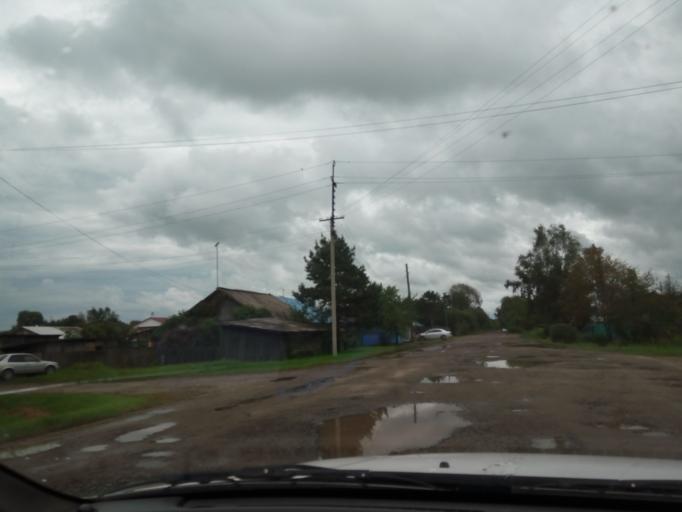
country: RU
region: Primorskiy
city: Dal'nerechensk
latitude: 45.9178
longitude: 133.7229
